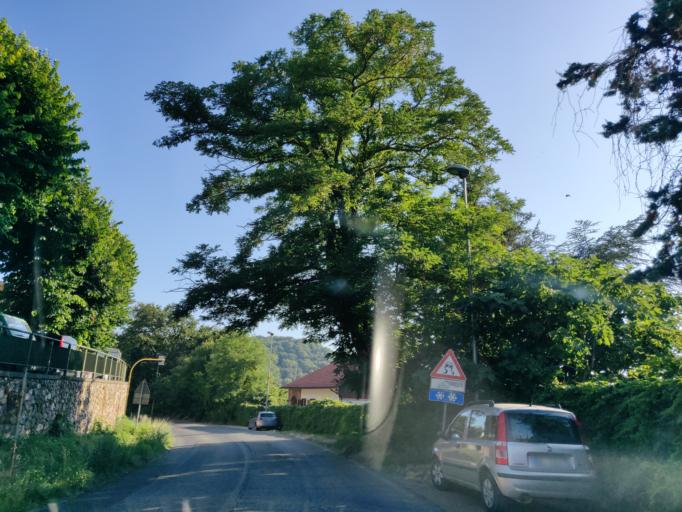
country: IT
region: Latium
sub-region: Citta metropolitana di Roma Capitale
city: Allumiere
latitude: 42.1576
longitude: 11.9074
